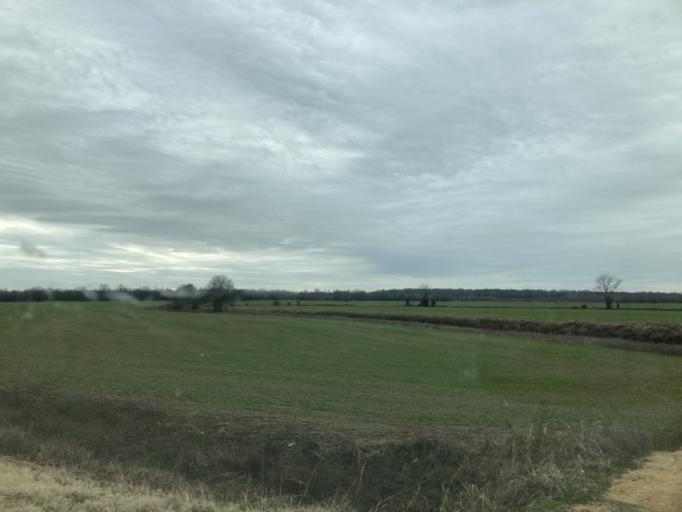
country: US
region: Mississippi
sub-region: Yazoo County
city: Yazoo City
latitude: 32.9813
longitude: -90.4614
